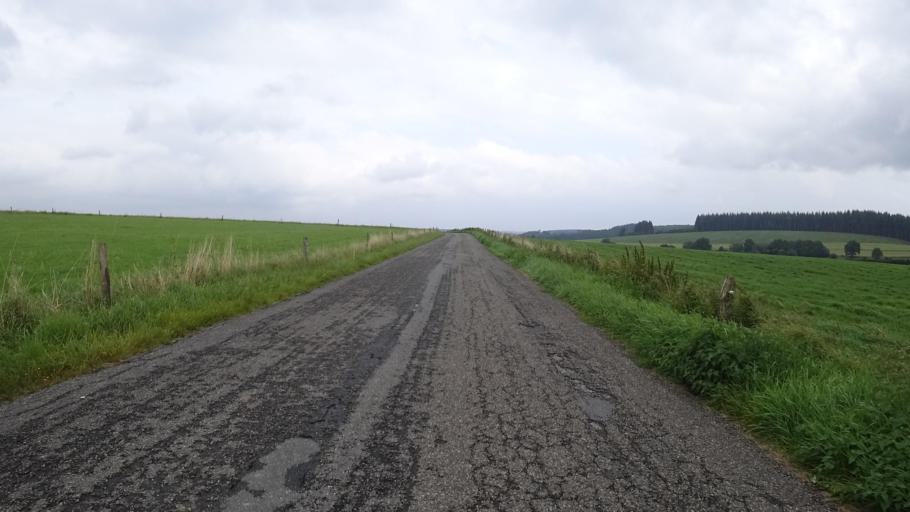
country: BE
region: Wallonia
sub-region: Province du Luxembourg
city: Chiny
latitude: 49.8075
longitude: 5.3424
